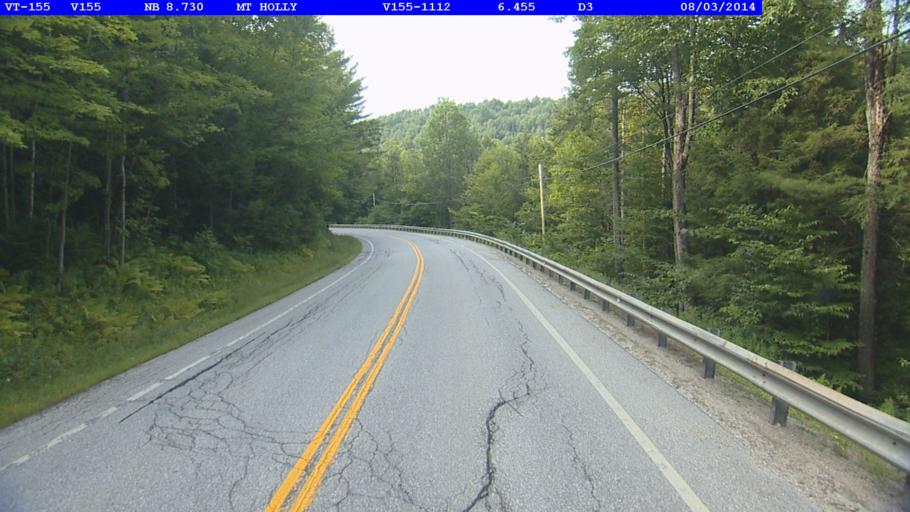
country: US
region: Vermont
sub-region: Rutland County
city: Rutland
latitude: 43.4360
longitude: -72.8582
